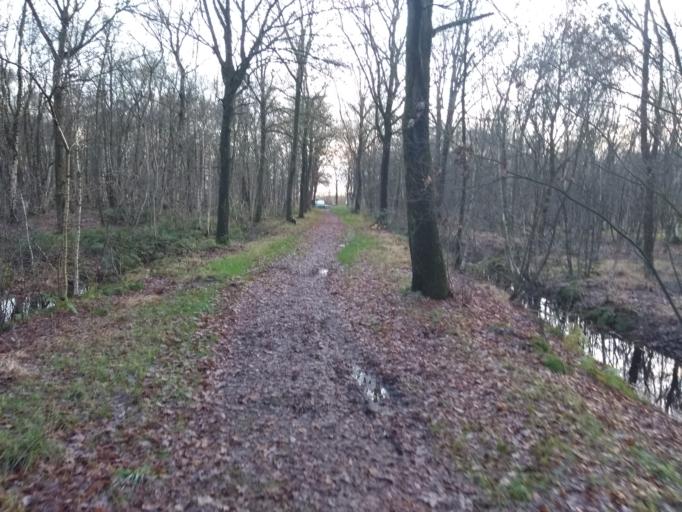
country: NL
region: Overijssel
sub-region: Gemeente Twenterand
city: Westerhaar-Vriezenveensewijk
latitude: 52.4458
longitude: 6.6761
